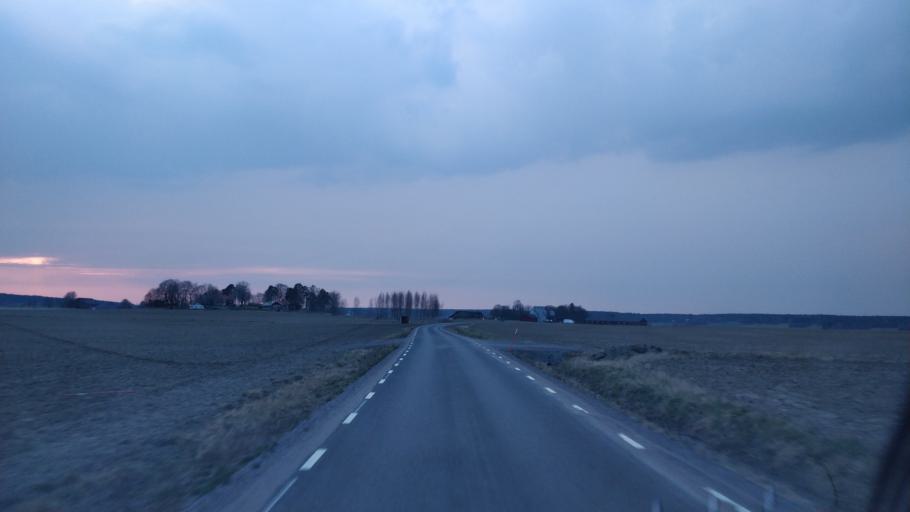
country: SE
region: Uppsala
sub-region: Enkopings Kommun
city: Orsundsbro
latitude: 59.7271
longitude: 17.2165
